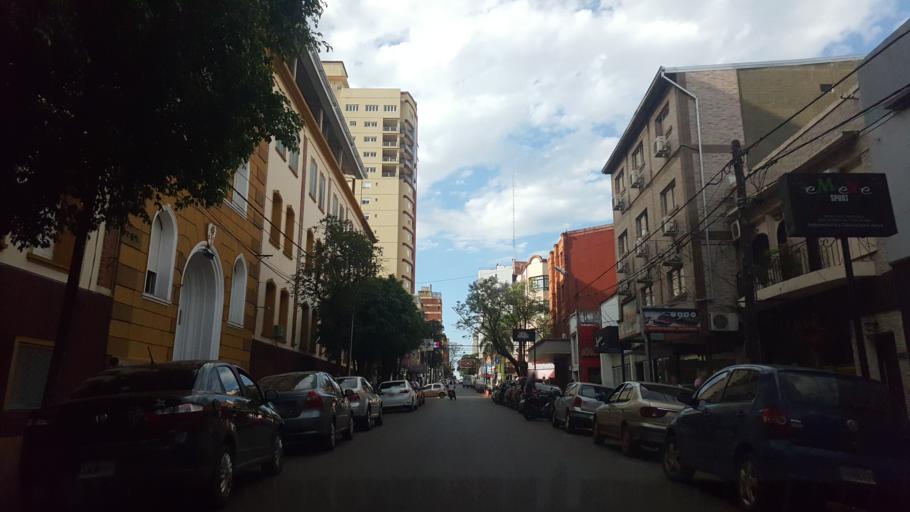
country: AR
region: Misiones
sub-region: Departamento de Capital
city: Posadas
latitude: -27.3694
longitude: -55.8950
